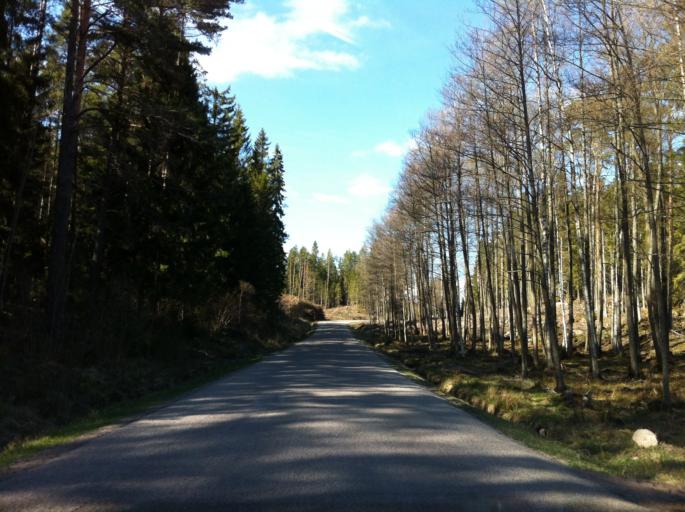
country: SE
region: Kalmar
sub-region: Vimmerby Kommun
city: Sodra Vi
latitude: 57.7856
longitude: 15.8591
